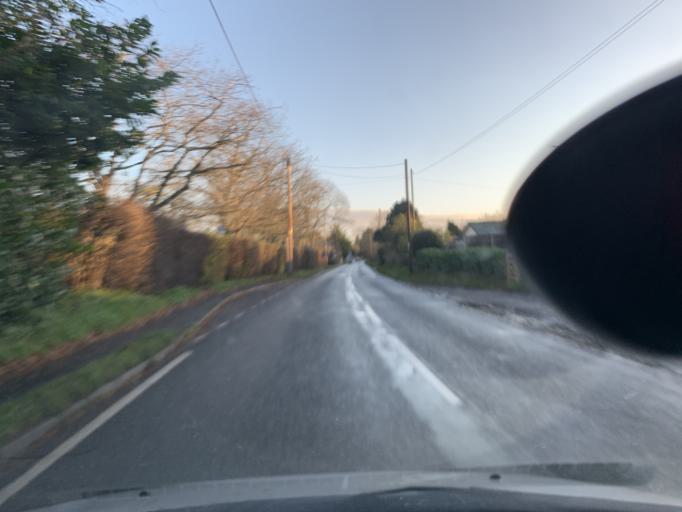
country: GB
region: England
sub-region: Hampshire
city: Fordingbridge
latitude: 50.9303
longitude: -1.7597
